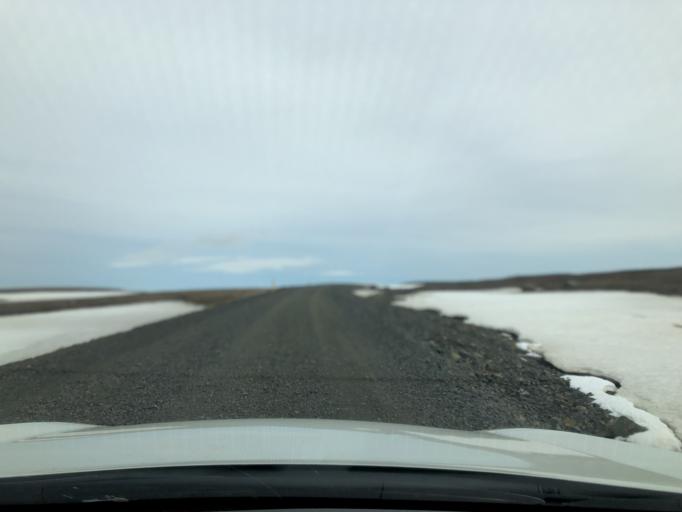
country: IS
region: East
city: Egilsstadir
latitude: 65.3063
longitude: -15.3927
